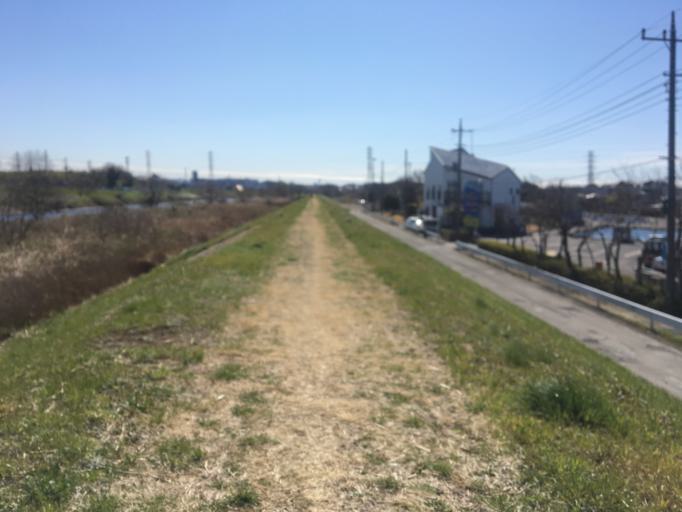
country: JP
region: Saitama
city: Asaka
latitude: 35.8180
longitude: 139.6083
